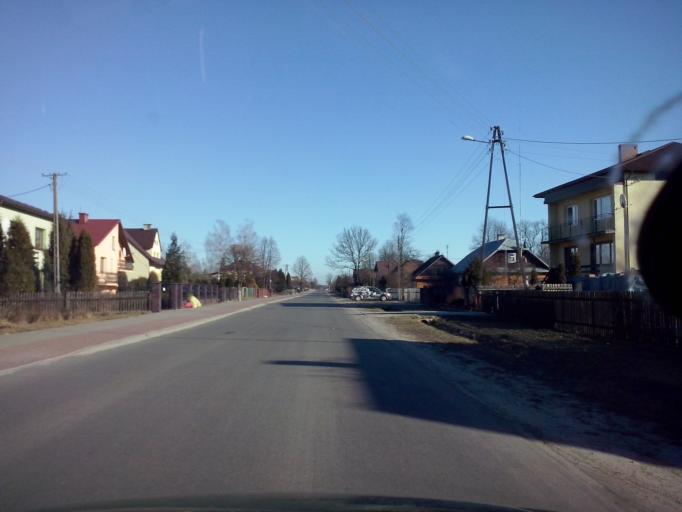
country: PL
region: Subcarpathian Voivodeship
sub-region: Powiat nizanski
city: Harasiuki
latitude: 50.4741
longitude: 22.4787
